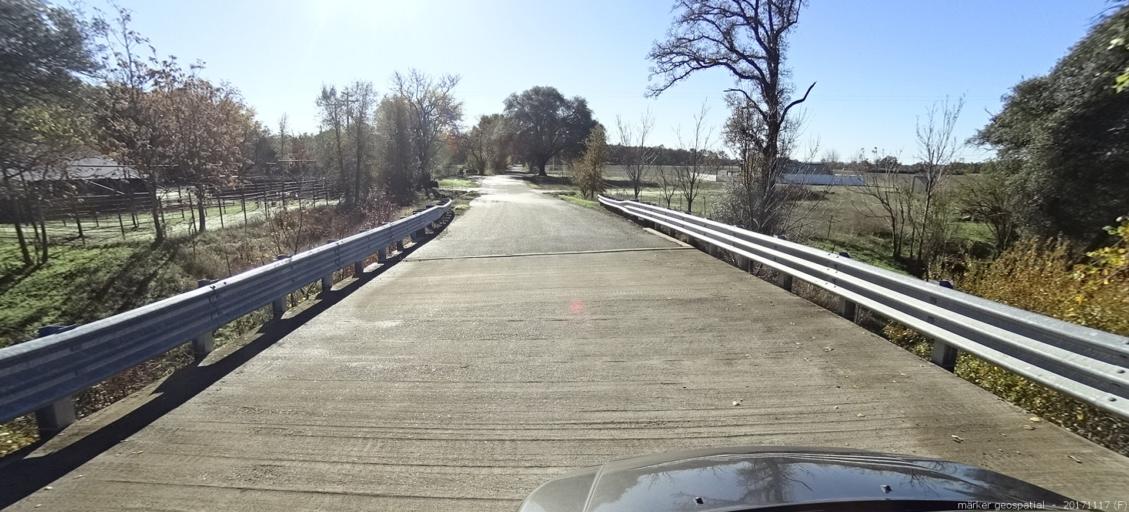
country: US
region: California
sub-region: Shasta County
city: Anderson
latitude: 40.4480
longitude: -122.1973
